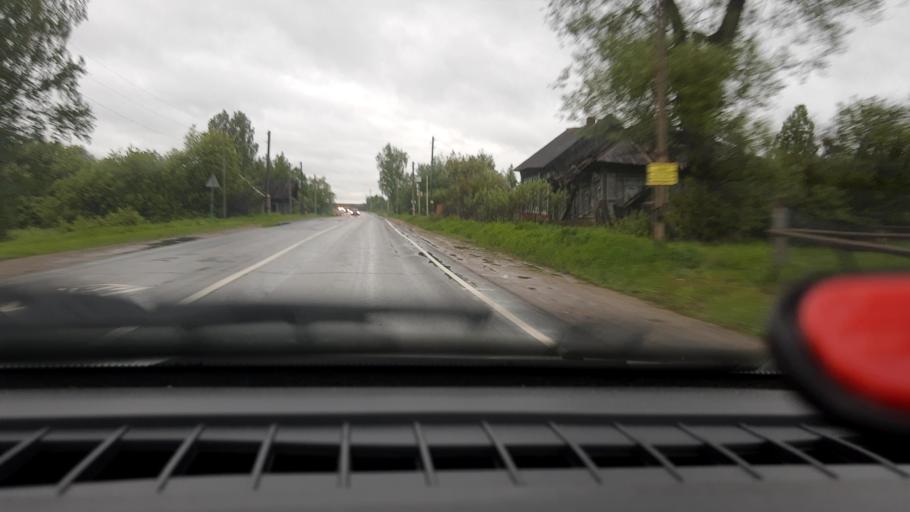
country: RU
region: Nizjnij Novgorod
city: Krasnyye Baki
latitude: 57.0123
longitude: 45.1136
